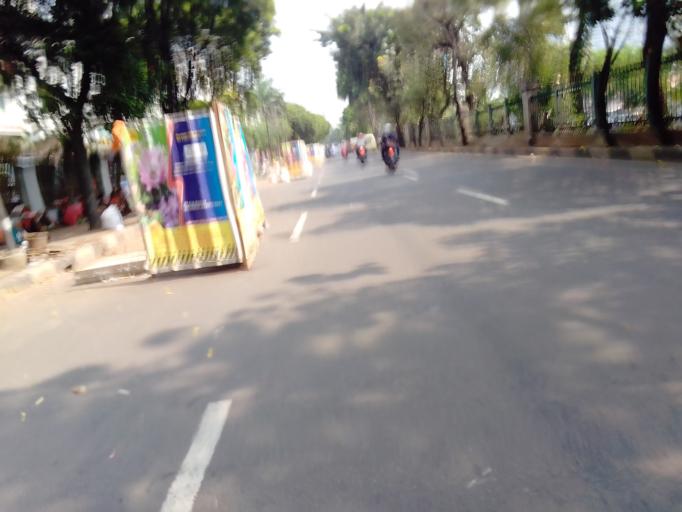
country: ID
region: Jakarta Raya
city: Jakarta
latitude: -6.2203
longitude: 106.7916
